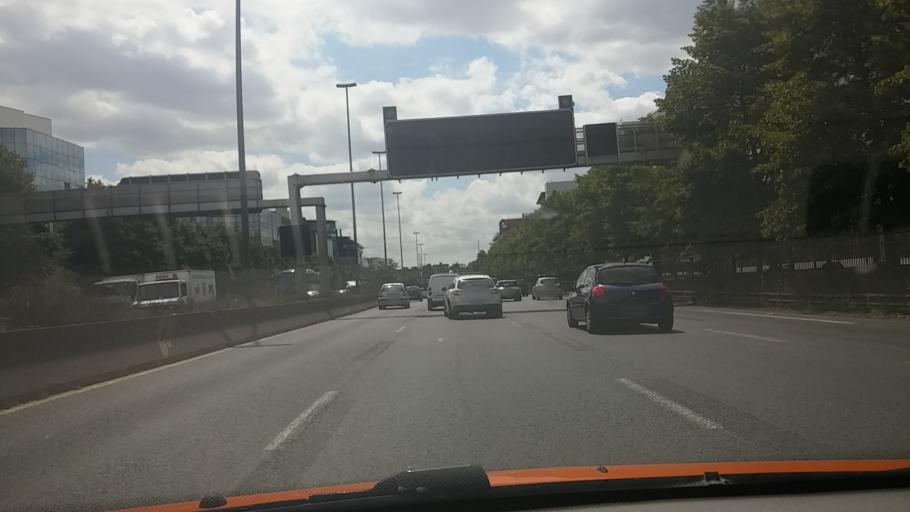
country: FR
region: Ile-de-France
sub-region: Departement de Seine-Saint-Denis
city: Saint-Denis
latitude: 48.9207
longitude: 2.3574
